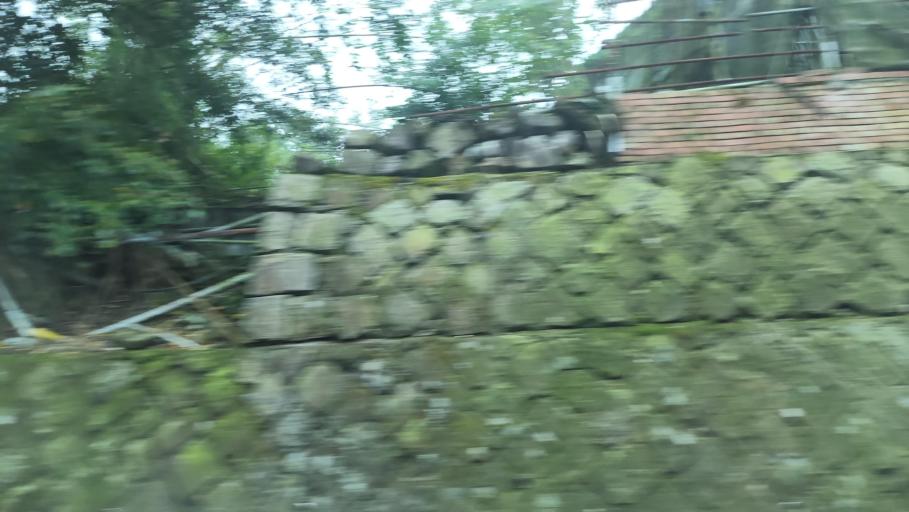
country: TW
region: Taipei
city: Taipei
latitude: 25.1455
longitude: 121.6040
